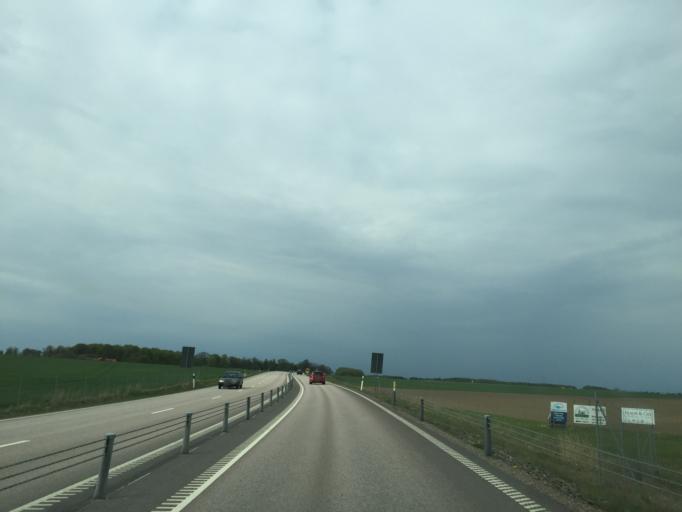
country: SE
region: Skane
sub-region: Helsingborg
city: Helsingborg
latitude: 56.1089
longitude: 12.6517
